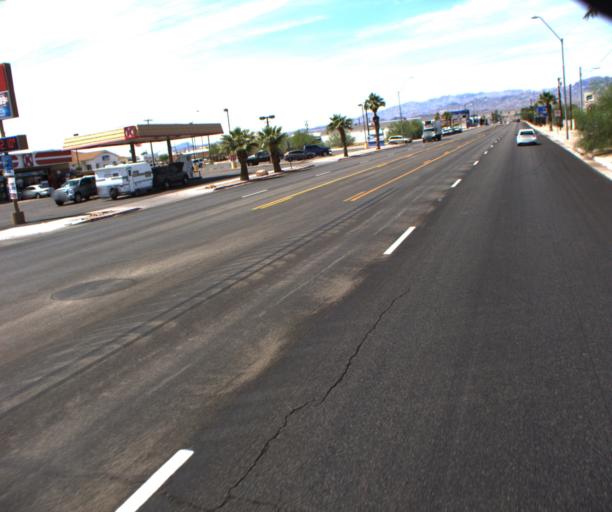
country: US
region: Arizona
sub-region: La Paz County
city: Parker
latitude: 34.1444
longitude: -114.2853
